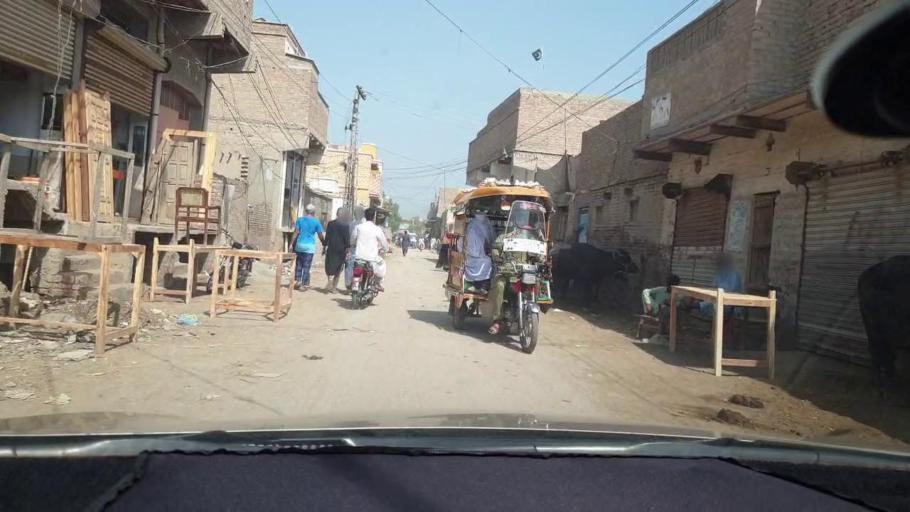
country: PK
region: Sindh
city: Kambar
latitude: 27.5838
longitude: 68.0028
